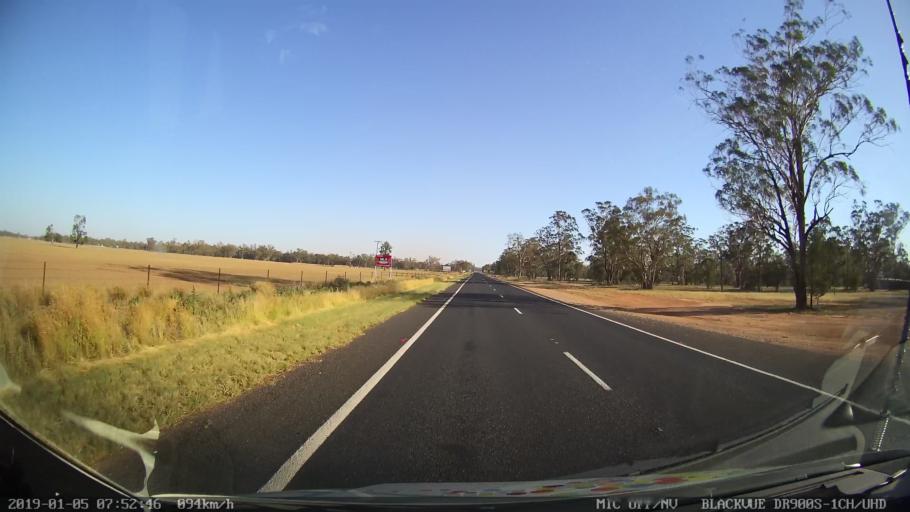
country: AU
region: New South Wales
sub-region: Gilgandra
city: Gilgandra
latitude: -31.7537
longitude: 148.6406
